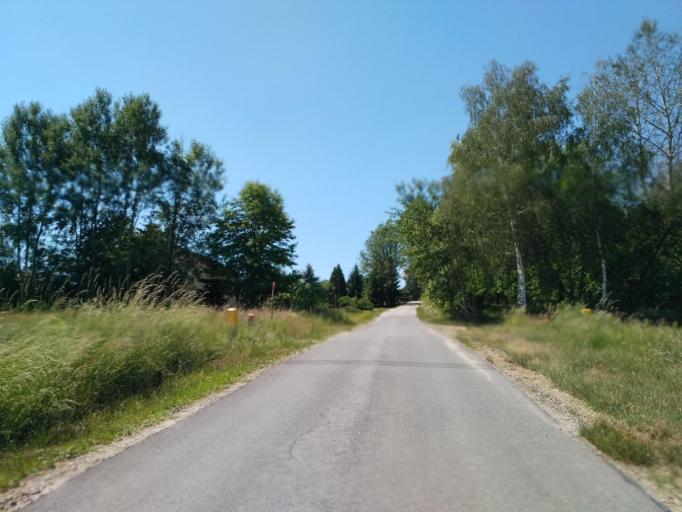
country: PL
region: Subcarpathian Voivodeship
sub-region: Krosno
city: Krosno
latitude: 49.7132
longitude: 21.7757
